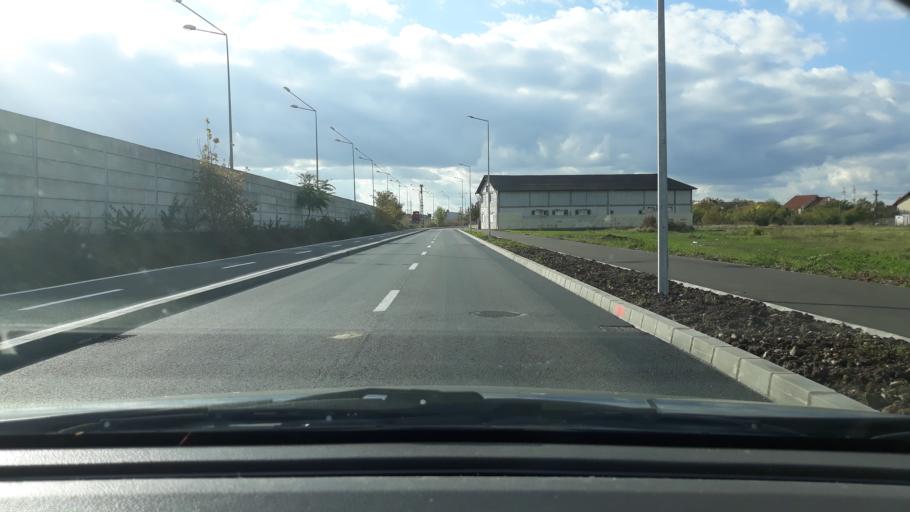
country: RO
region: Bihor
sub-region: Comuna Sanmartin
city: Sanmartin
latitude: 47.0251
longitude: 21.9525
